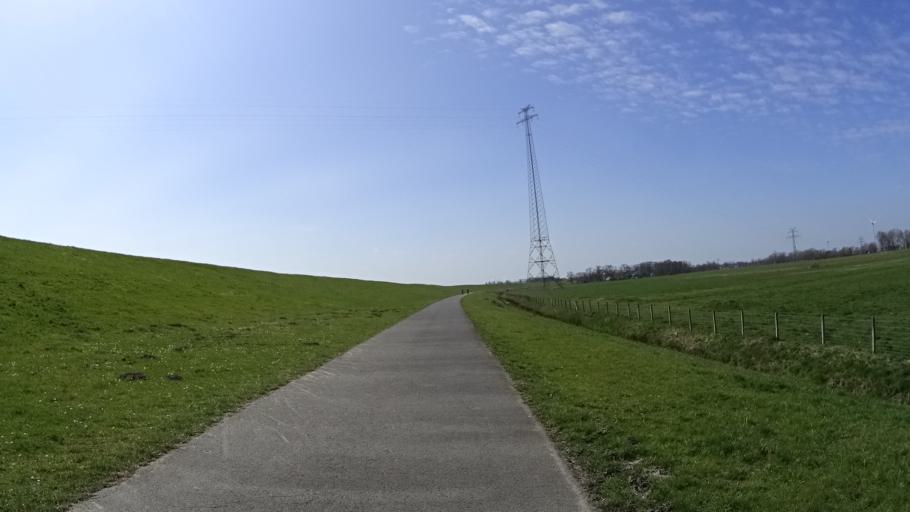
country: DE
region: Lower Saxony
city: Weener
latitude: 53.1797
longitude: 7.3847
